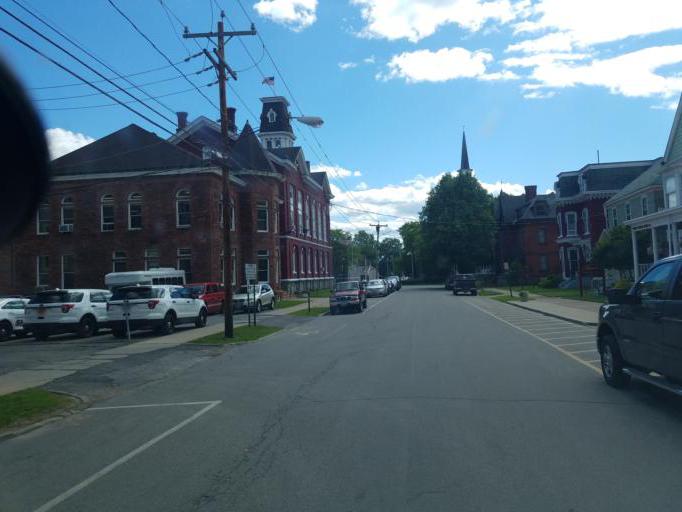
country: US
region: New York
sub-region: Herkimer County
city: Herkimer
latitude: 43.0297
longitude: -74.9884
